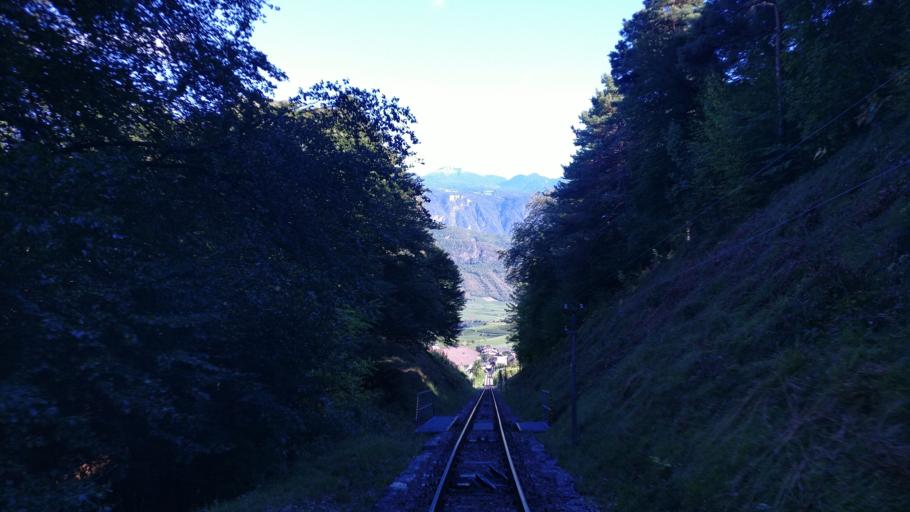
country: IT
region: Trentino-Alto Adige
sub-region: Bolzano
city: Caldaro sulla Strada del Vino
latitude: 46.4103
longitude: 11.2289
